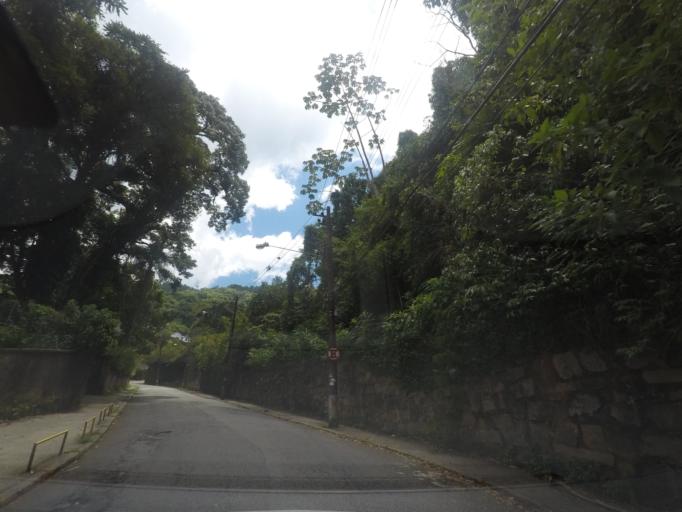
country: BR
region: Rio de Janeiro
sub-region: Petropolis
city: Petropolis
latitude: -22.5025
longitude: -43.1850
